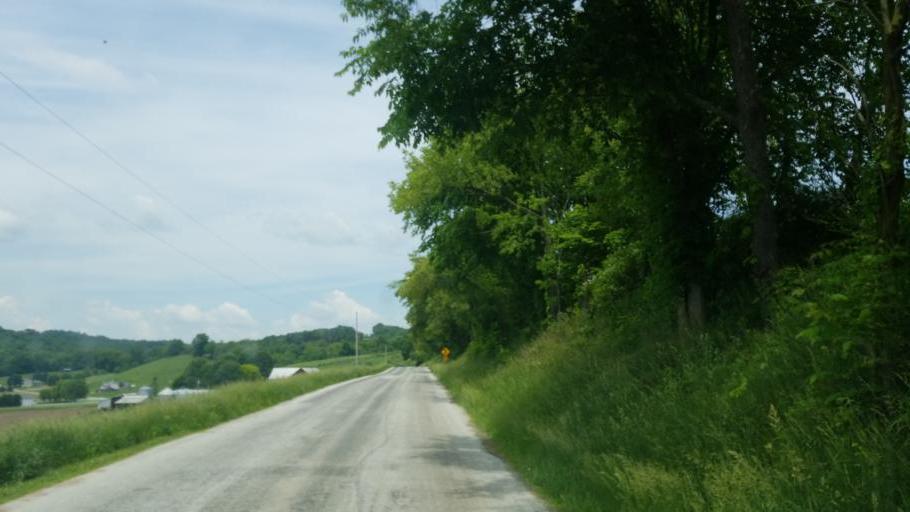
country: US
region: Ohio
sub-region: Coshocton County
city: West Lafayette
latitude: 40.3765
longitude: -81.7576
